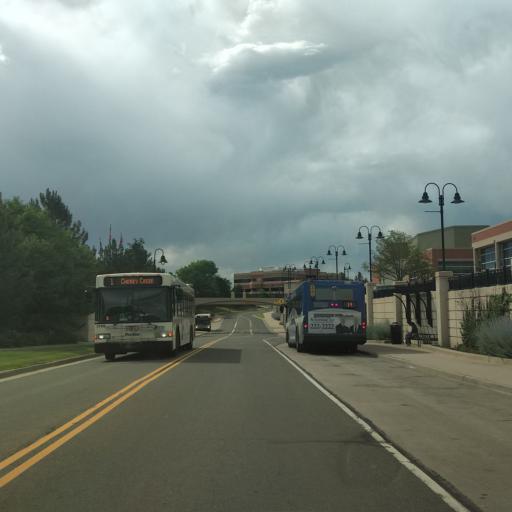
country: US
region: Colorado
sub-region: Jefferson County
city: Lakewood
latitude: 39.7073
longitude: -105.0845
